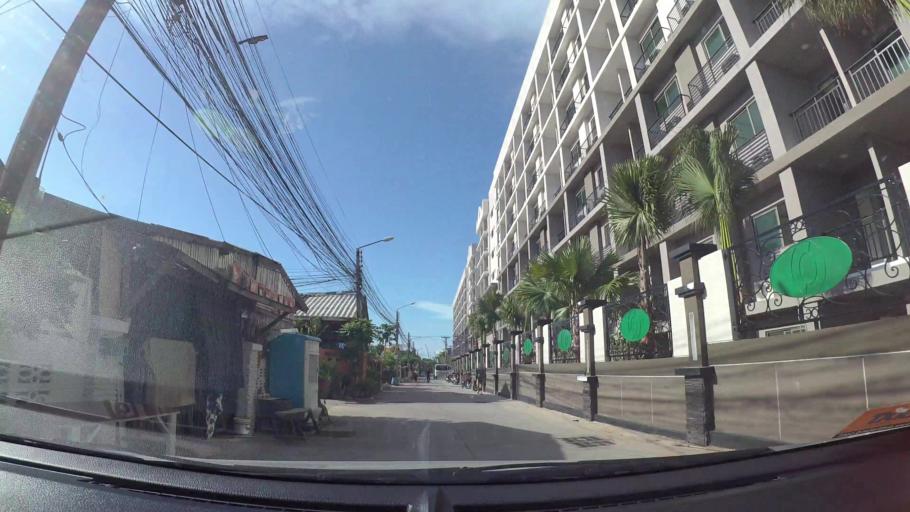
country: TH
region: Chon Buri
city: Phatthaya
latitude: 12.9141
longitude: 100.8736
